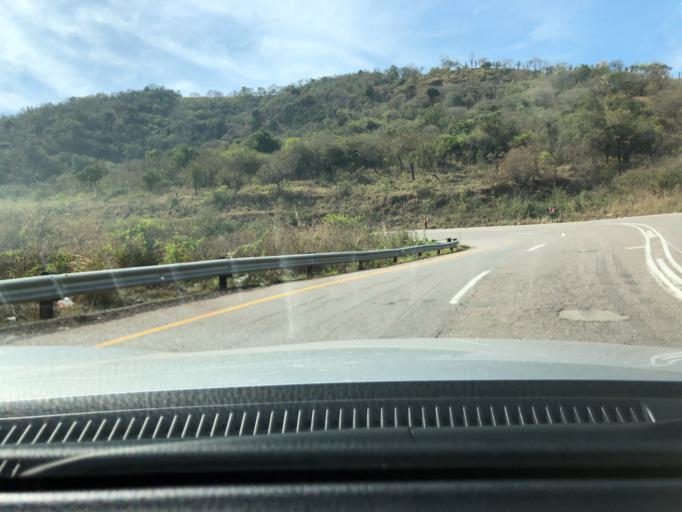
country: ZA
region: KwaZulu-Natal
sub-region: uMgungundlovu District Municipality
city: Richmond
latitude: -29.9976
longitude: 30.2452
